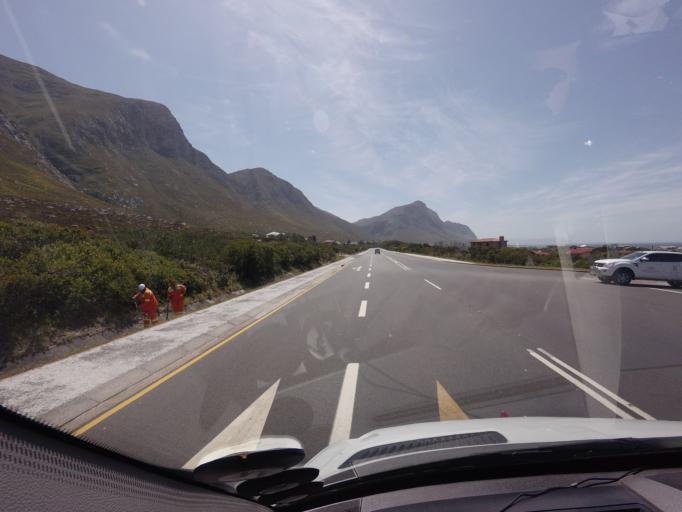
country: ZA
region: Western Cape
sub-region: Overberg District Municipality
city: Grabouw
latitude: -34.3561
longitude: 18.8994
